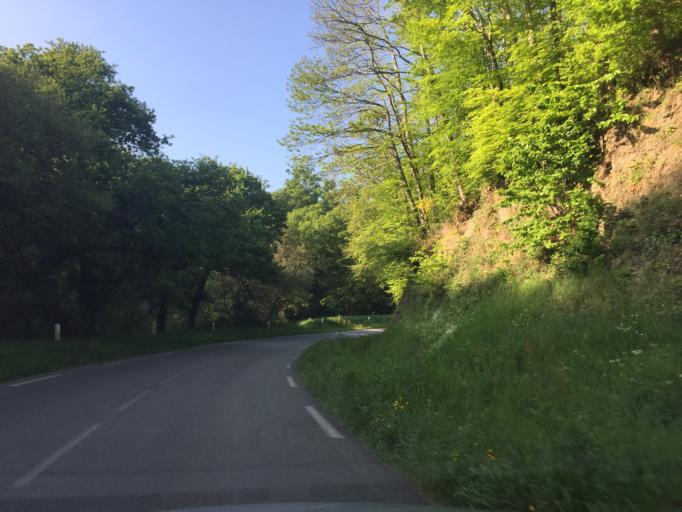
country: FR
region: Brittany
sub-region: Departement des Cotes-d'Armor
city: Crehen
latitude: 48.5737
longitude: -2.2399
